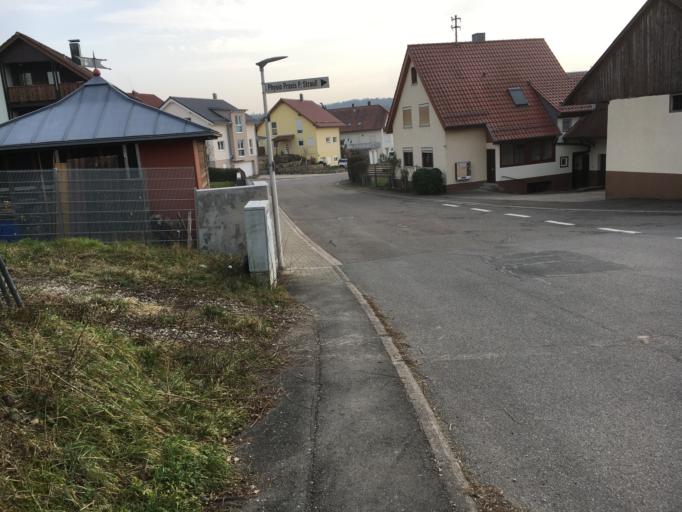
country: DE
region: Baden-Wuerttemberg
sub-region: Karlsruhe Region
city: Limbach
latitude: 49.4028
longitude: 9.2206
